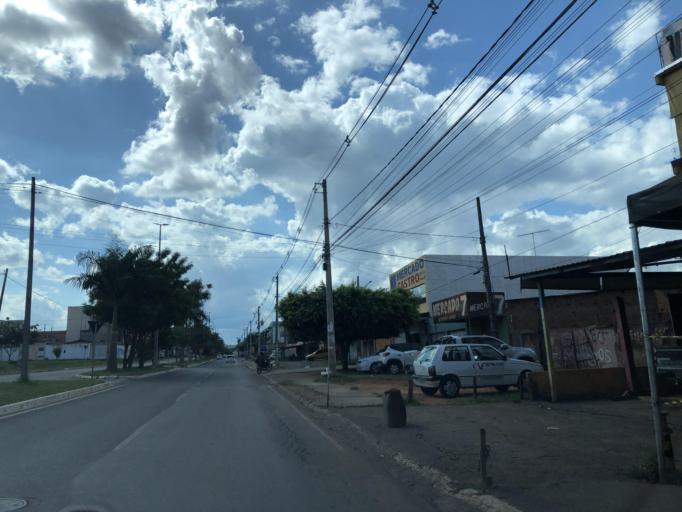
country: BR
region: Federal District
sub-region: Brasilia
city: Brasilia
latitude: -15.8950
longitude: -47.7766
